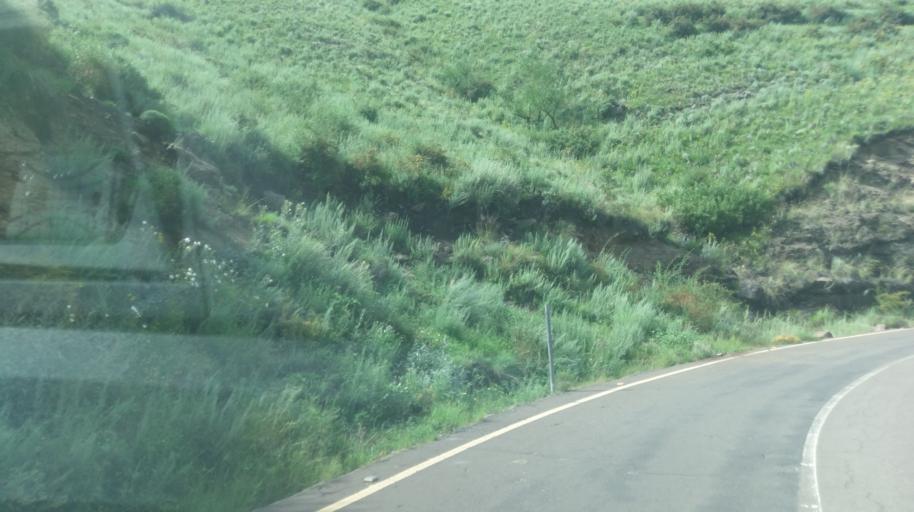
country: LS
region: Thaba-Tseka
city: Thaba-Tseka
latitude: -29.1517
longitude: 28.4796
